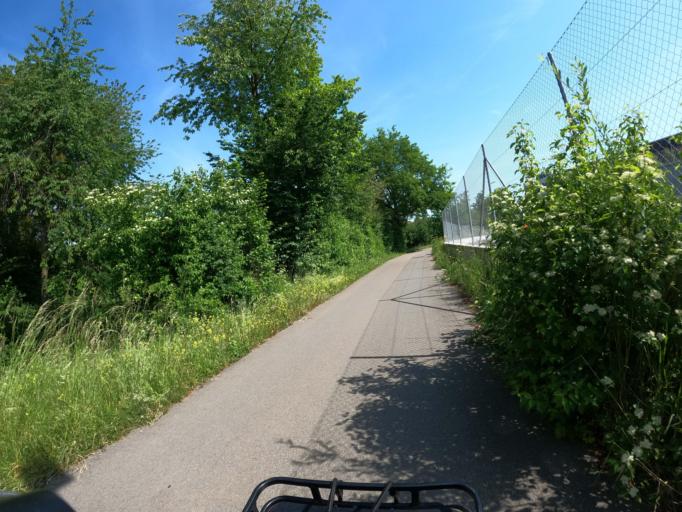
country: CH
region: Zurich
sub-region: Bezirk Dielsdorf
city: Niederglatt
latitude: 47.5006
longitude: 8.4938
